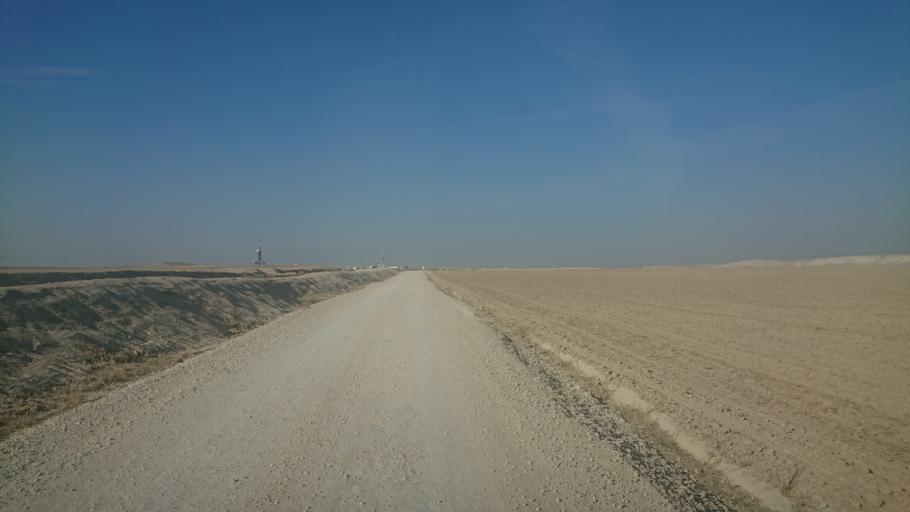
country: TR
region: Aksaray
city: Sultanhani
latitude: 38.0689
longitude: 33.6149
